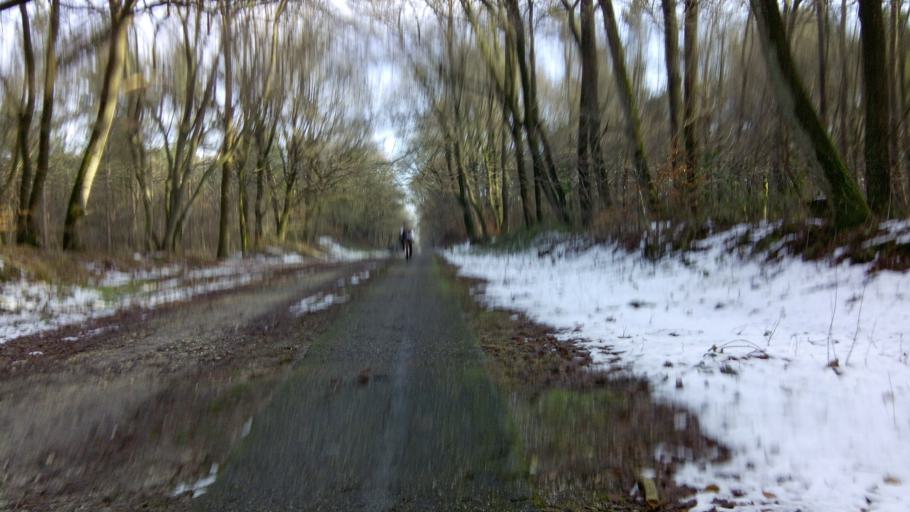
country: NL
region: Gelderland
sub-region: Gemeente Groesbeek
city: Groesbeek
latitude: 51.7867
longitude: 5.9013
